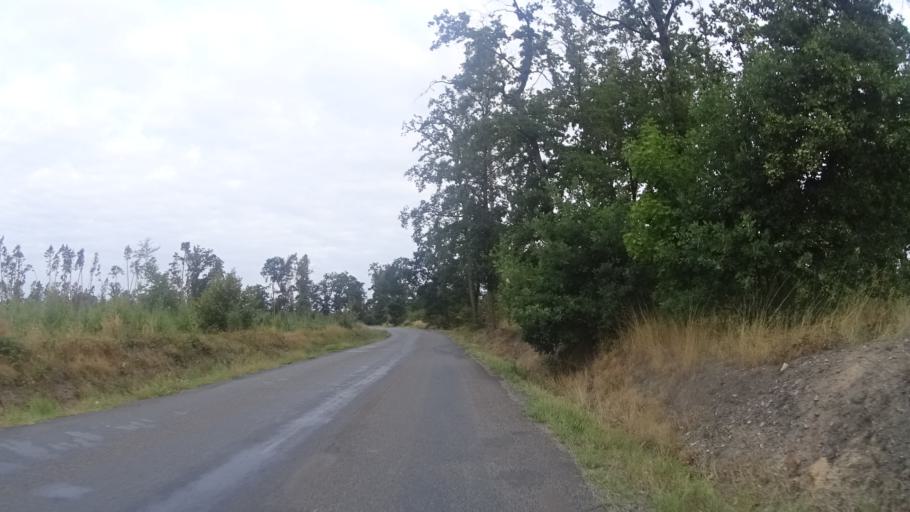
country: CZ
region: Kralovehradecky
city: Cernilov
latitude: 50.2079
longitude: 15.9216
